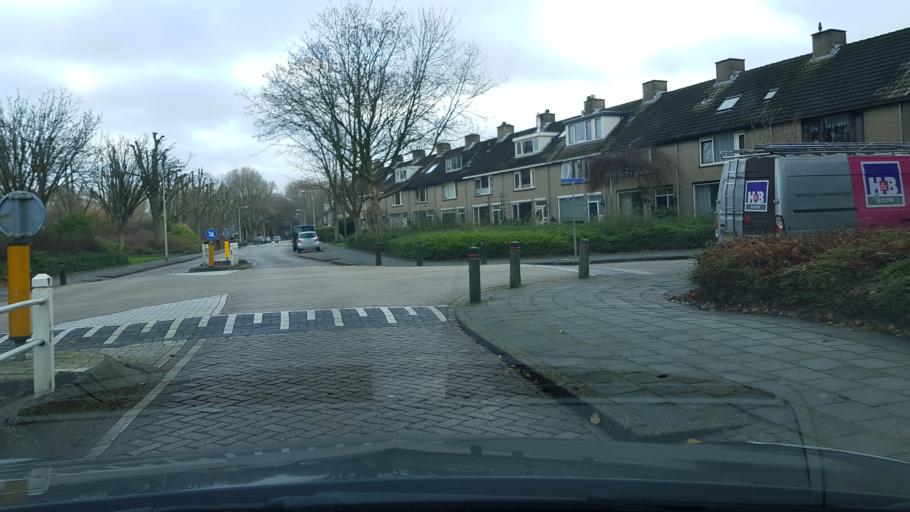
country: NL
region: South Holland
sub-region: Gemeente Lisse
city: Lisse
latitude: 52.2470
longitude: 4.5588
